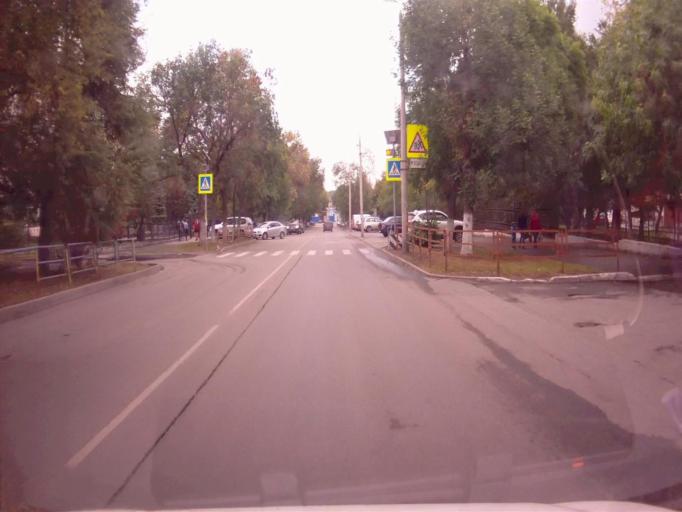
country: RU
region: Chelyabinsk
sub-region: Gorod Chelyabinsk
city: Chelyabinsk
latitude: 55.1587
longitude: 61.4179
